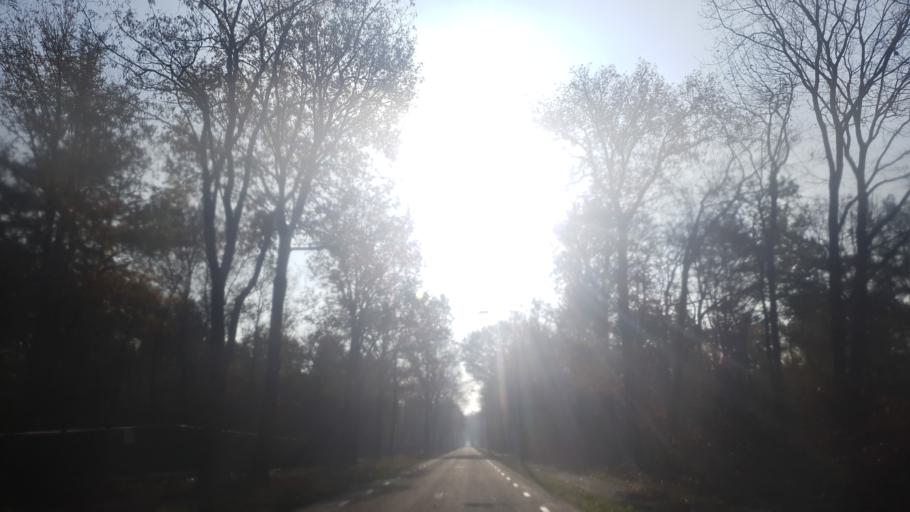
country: NL
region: North Brabant
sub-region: Gemeente Landerd
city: Reek
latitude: 51.7306
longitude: 5.6821
